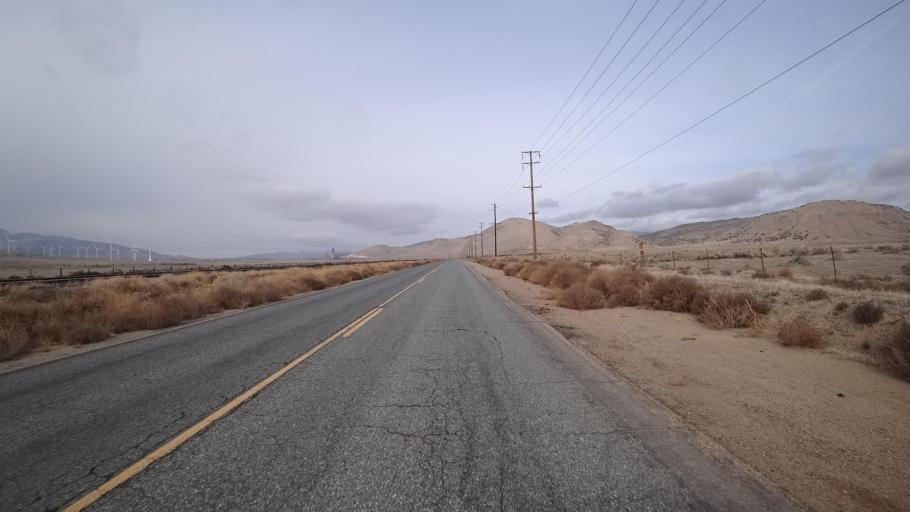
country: US
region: California
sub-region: Kern County
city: Tehachapi
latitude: 35.1149
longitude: -118.3299
